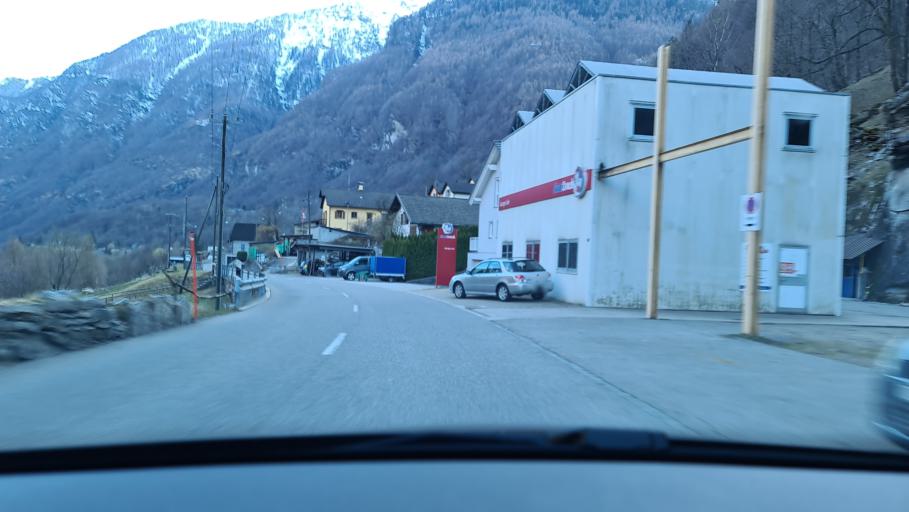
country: CH
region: Ticino
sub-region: Locarno District
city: Lavertezzo
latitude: 46.3005
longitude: 8.7927
